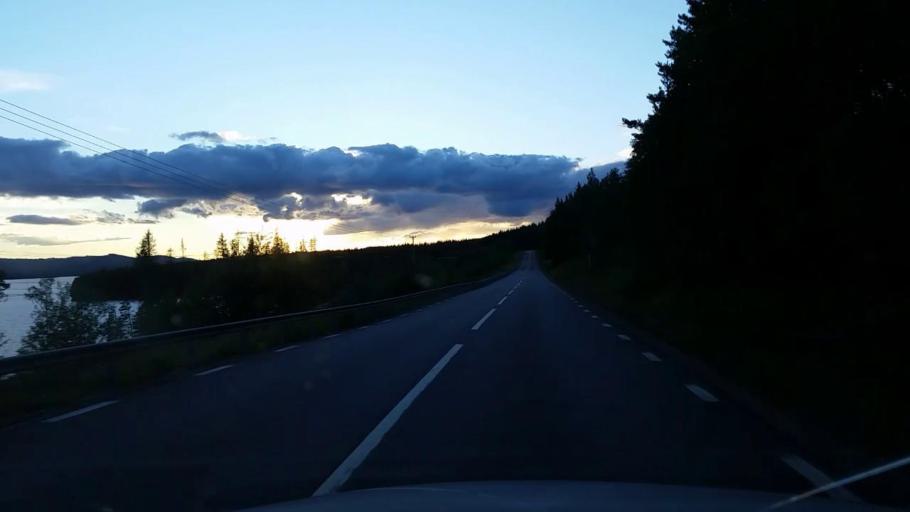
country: SE
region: Gaevleborg
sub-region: Ljusdals Kommun
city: Farila
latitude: 62.1045
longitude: 15.7750
